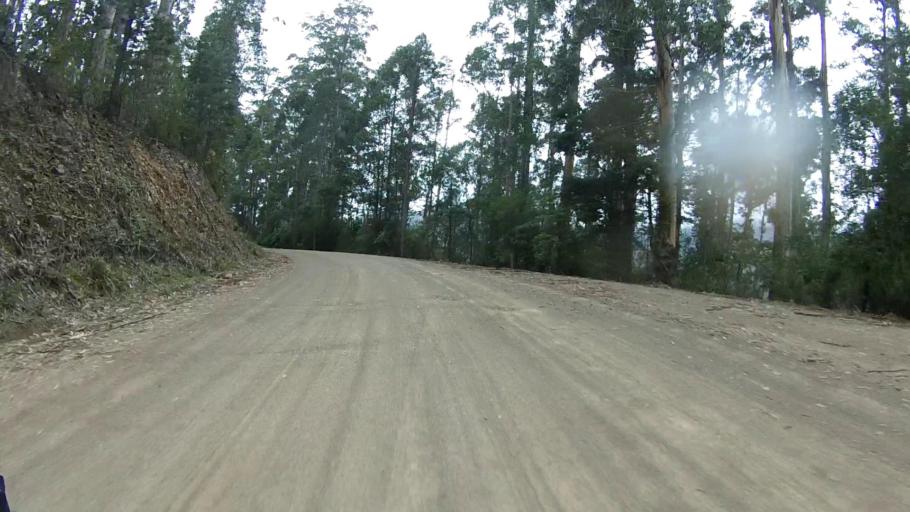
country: AU
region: Tasmania
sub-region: Sorell
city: Sorell
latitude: -42.6996
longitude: 147.8548
